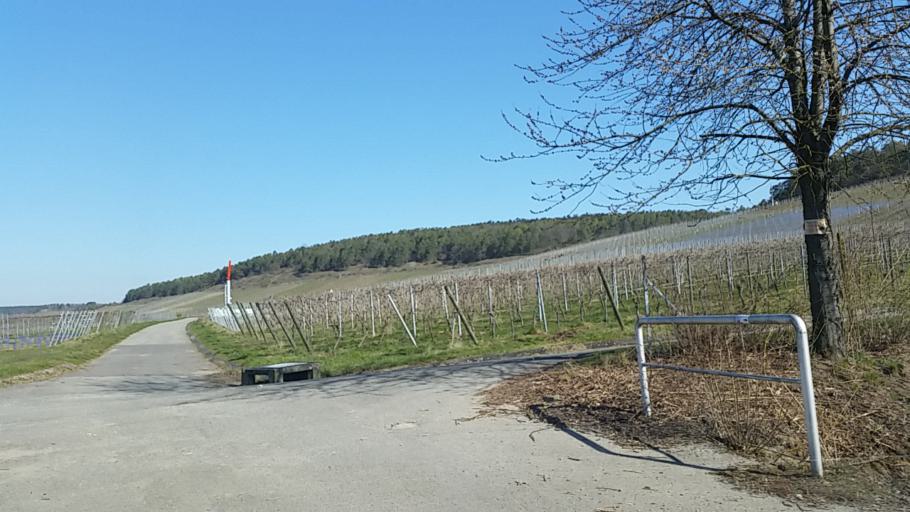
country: DE
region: Bavaria
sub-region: Regierungsbezirk Unterfranken
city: Himmelstadt
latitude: 49.9225
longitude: 9.8192
